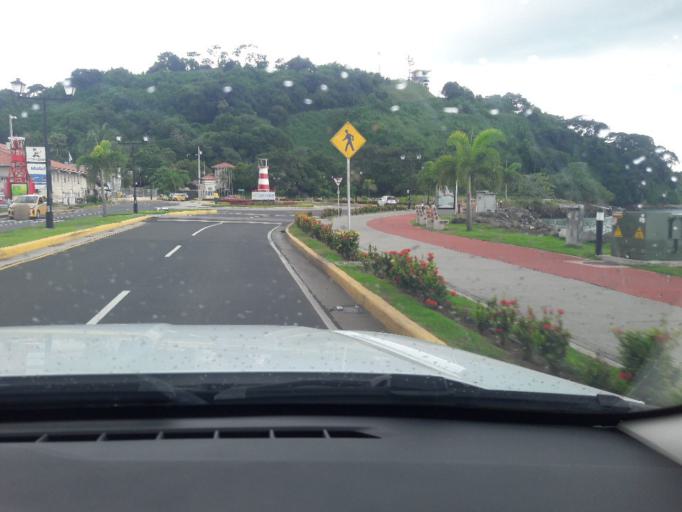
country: PA
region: Panama
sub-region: Distrito de Panama
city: Ancon
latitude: 8.9108
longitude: -79.5227
